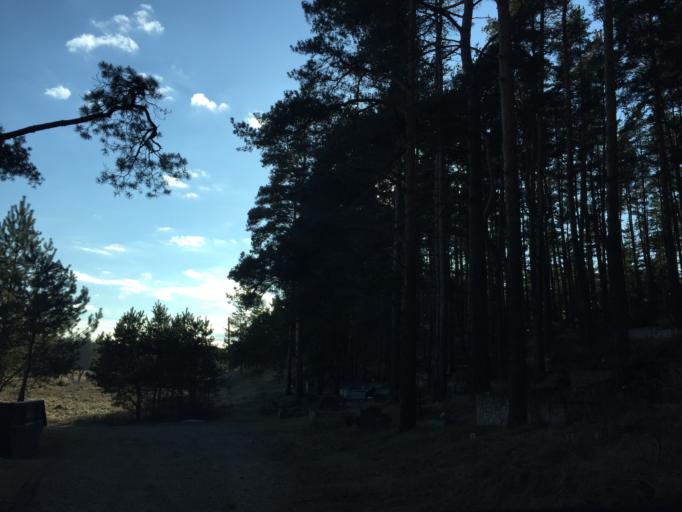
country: LV
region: Babite
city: Pinki
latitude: 56.9279
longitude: 23.9094
